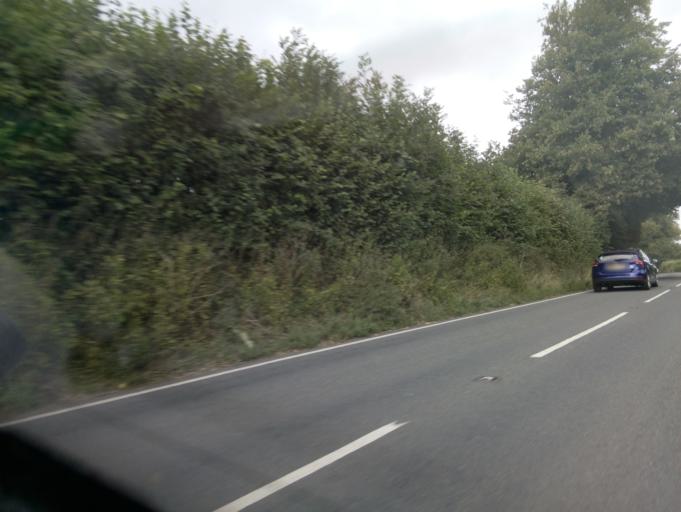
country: GB
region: England
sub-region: Devon
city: Exminster
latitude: 50.6618
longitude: -3.4846
